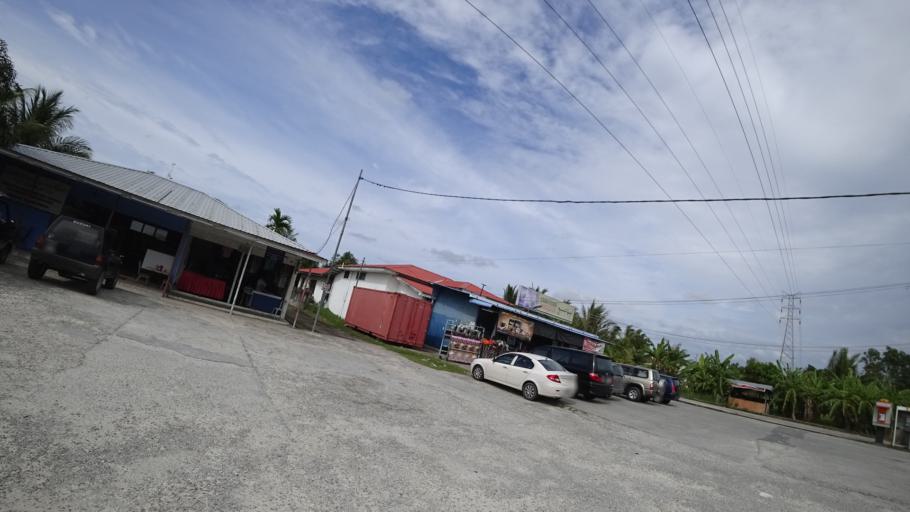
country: BN
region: Tutong
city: Tutong
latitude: 4.8217
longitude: 114.6834
